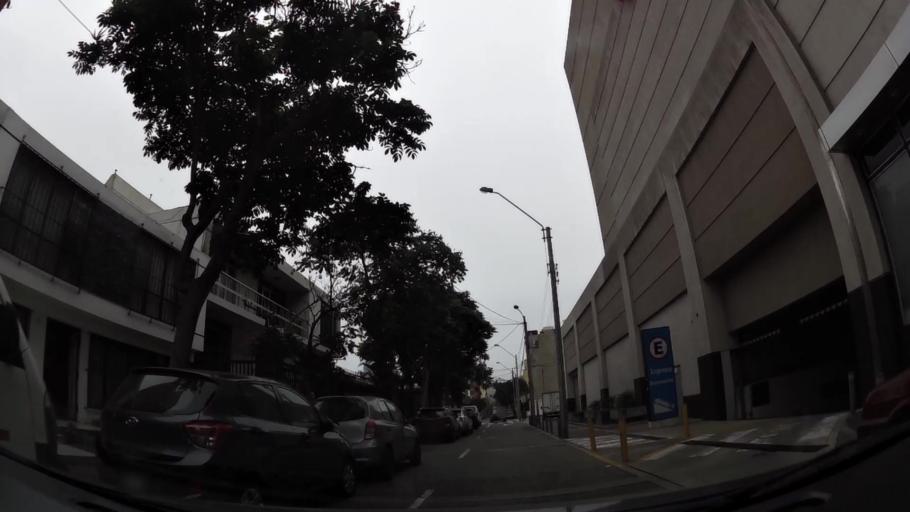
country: PE
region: Lima
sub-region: Lima
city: San Isidro
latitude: -12.1232
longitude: -77.0324
